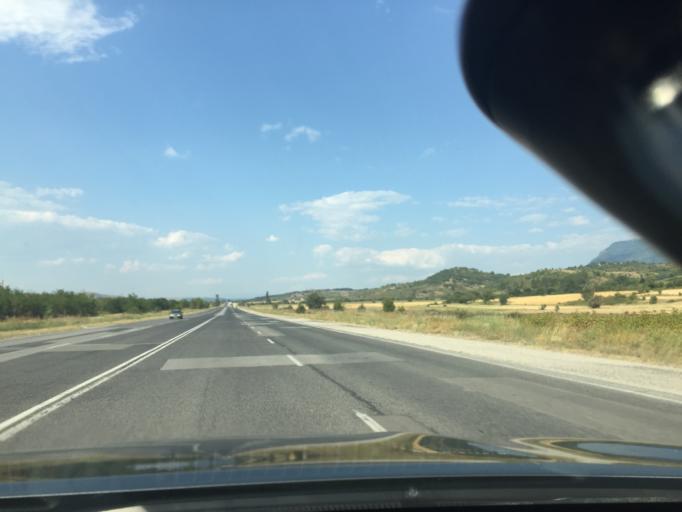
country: BG
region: Kyustendil
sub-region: Obshtina Boboshevo
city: Boboshevo
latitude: 42.1723
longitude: 23.0486
